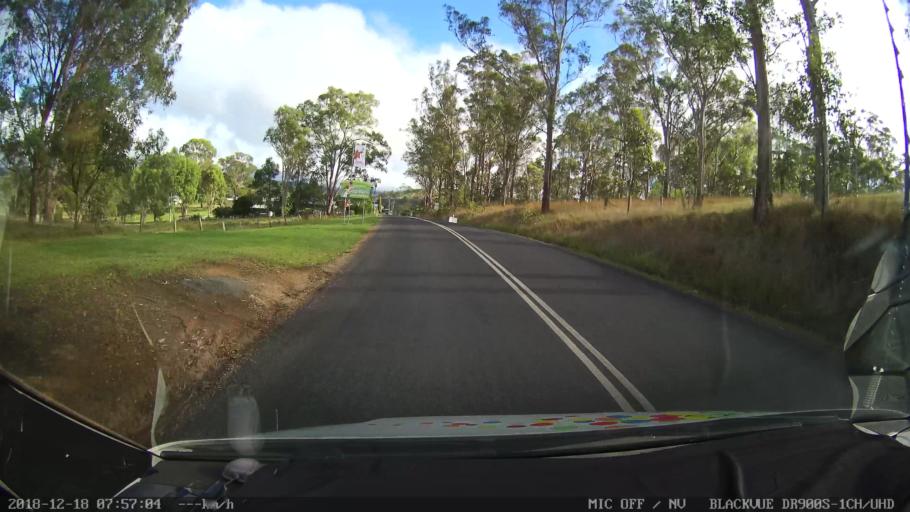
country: AU
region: New South Wales
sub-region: Kyogle
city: Kyogle
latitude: -28.3959
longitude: 152.6106
